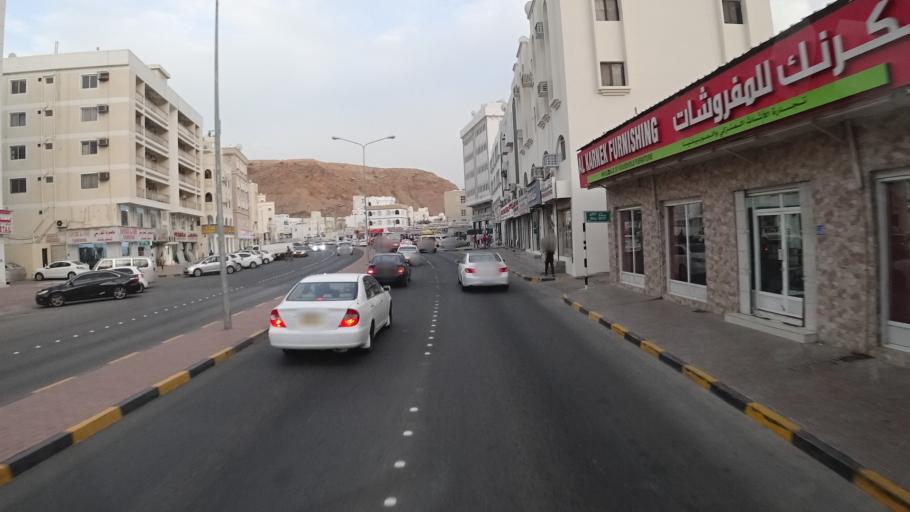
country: OM
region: Muhafazat Masqat
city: Muscat
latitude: 23.5828
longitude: 58.5415
